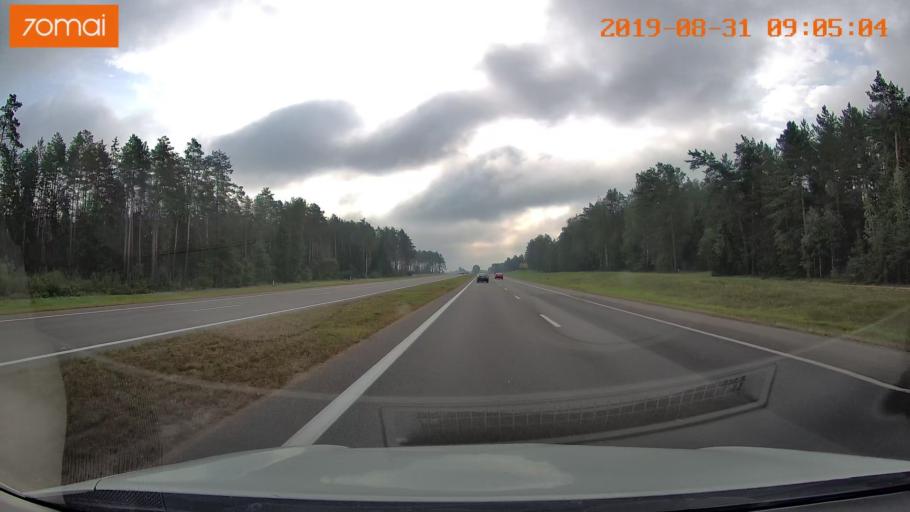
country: BY
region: Minsk
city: Chervyen'
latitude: 53.7281
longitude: 28.3645
